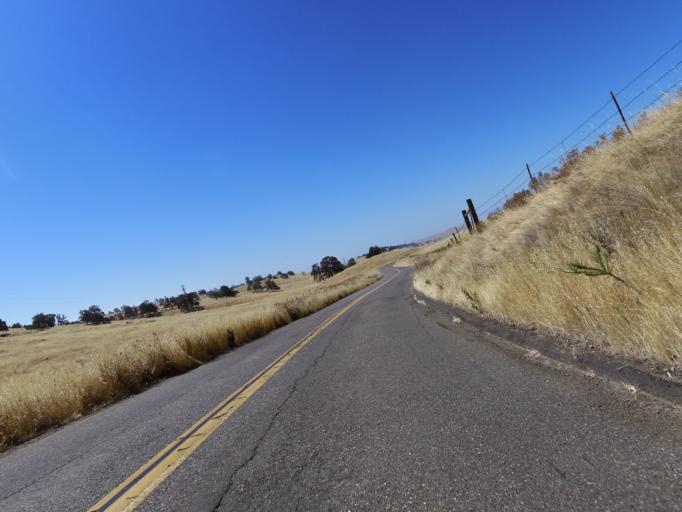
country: US
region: California
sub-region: Merced County
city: Planada
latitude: 37.5595
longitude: -120.3253
